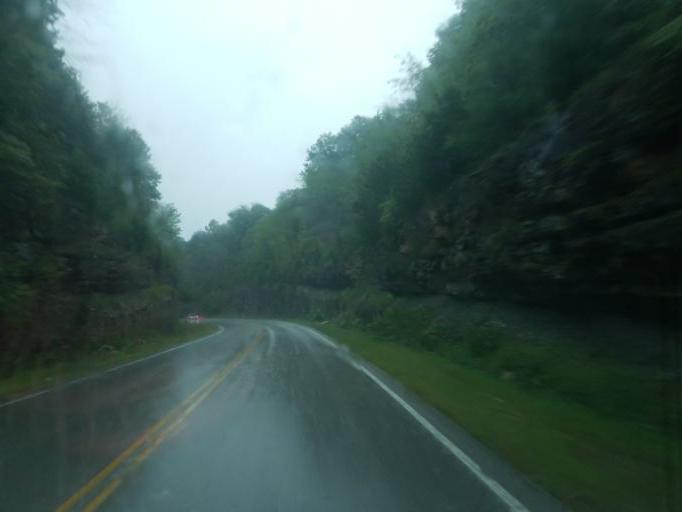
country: US
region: Kentucky
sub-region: Carter County
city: Olive Hill
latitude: 38.3348
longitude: -83.2054
